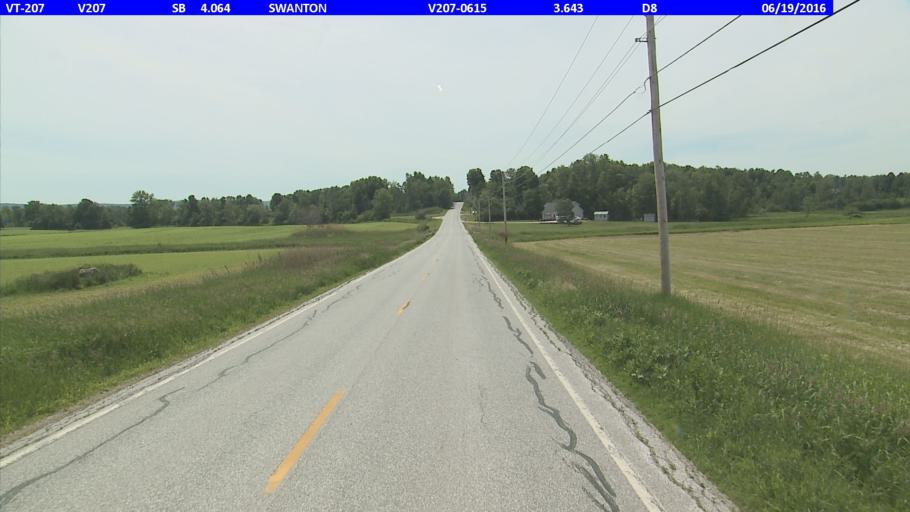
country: US
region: Vermont
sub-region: Franklin County
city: Swanton
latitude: 44.8965
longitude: -73.0671
